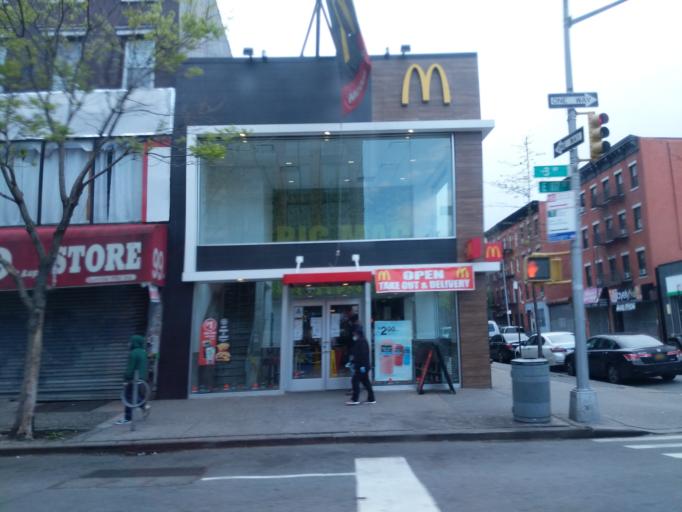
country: US
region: New York
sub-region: New York County
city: Manhattan
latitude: 40.7986
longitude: -73.9397
